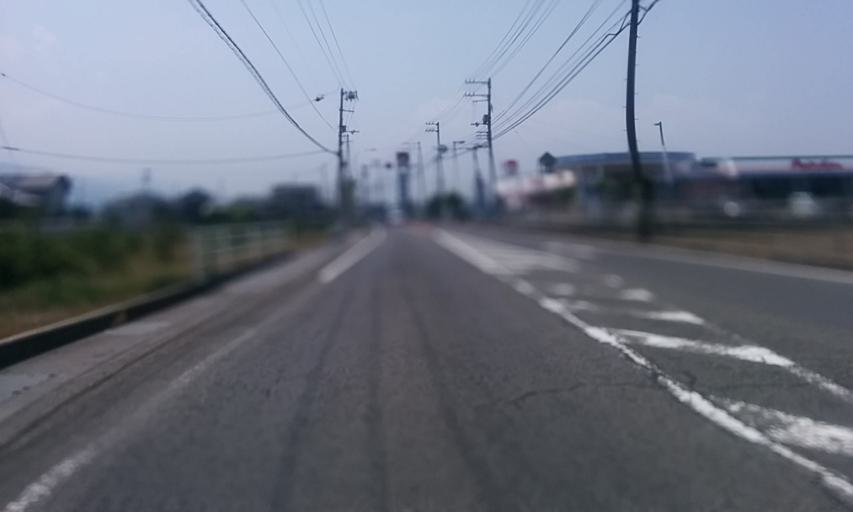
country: JP
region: Ehime
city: Saijo
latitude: 33.9120
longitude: 133.2016
